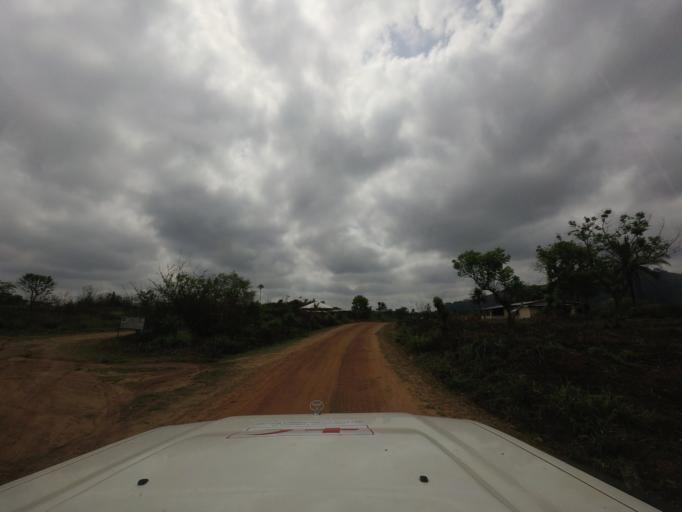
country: LR
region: Lofa
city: Voinjama
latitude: 8.4163
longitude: -9.7374
